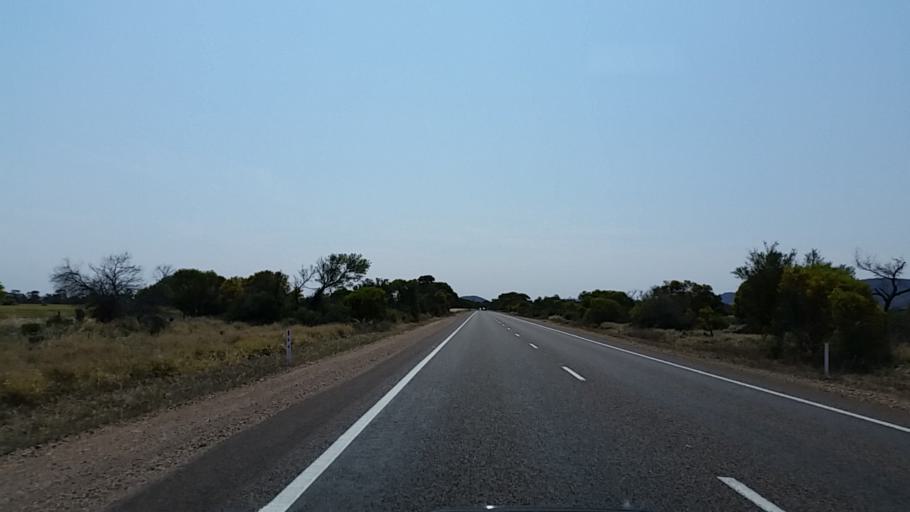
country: AU
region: South Australia
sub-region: Port Pirie City and Dists
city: Port Pirie
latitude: -32.8670
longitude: 137.9822
